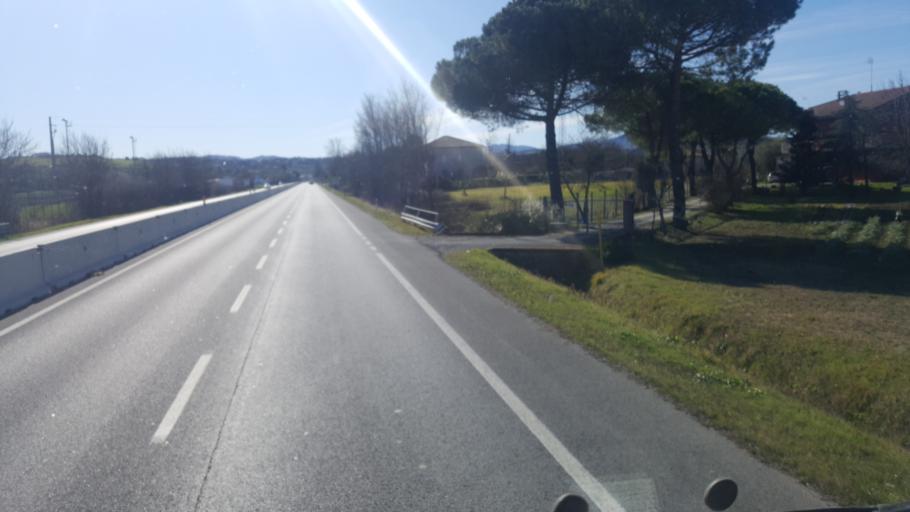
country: IT
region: Emilia-Romagna
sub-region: Provincia di Rimini
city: Cerasolo
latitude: 44.0099
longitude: 12.5454
